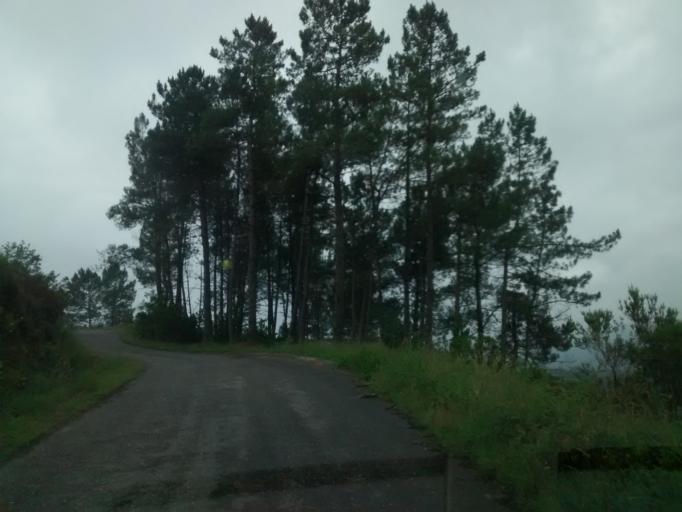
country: ES
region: Galicia
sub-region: Provincia de Ourense
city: Castro Caldelas
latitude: 42.4094
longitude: -7.3925
